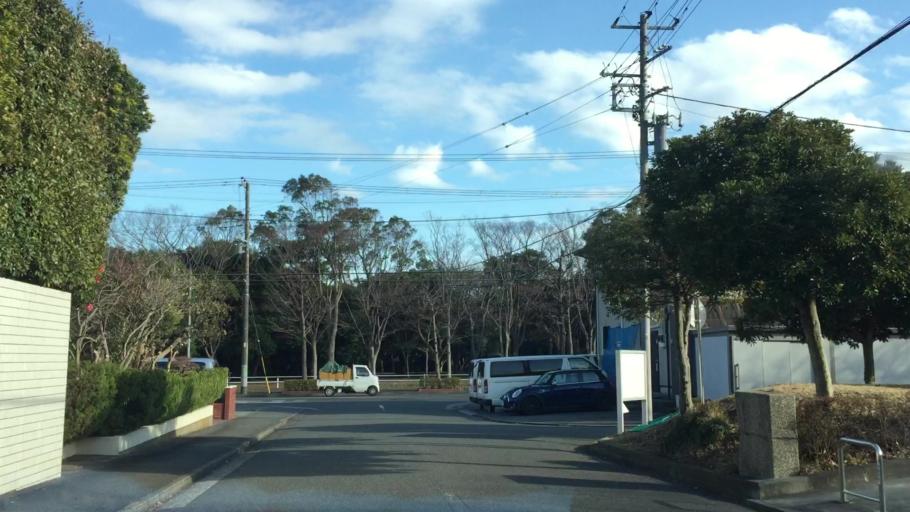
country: JP
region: Kanagawa
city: Zushi
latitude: 35.3385
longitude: 139.5949
